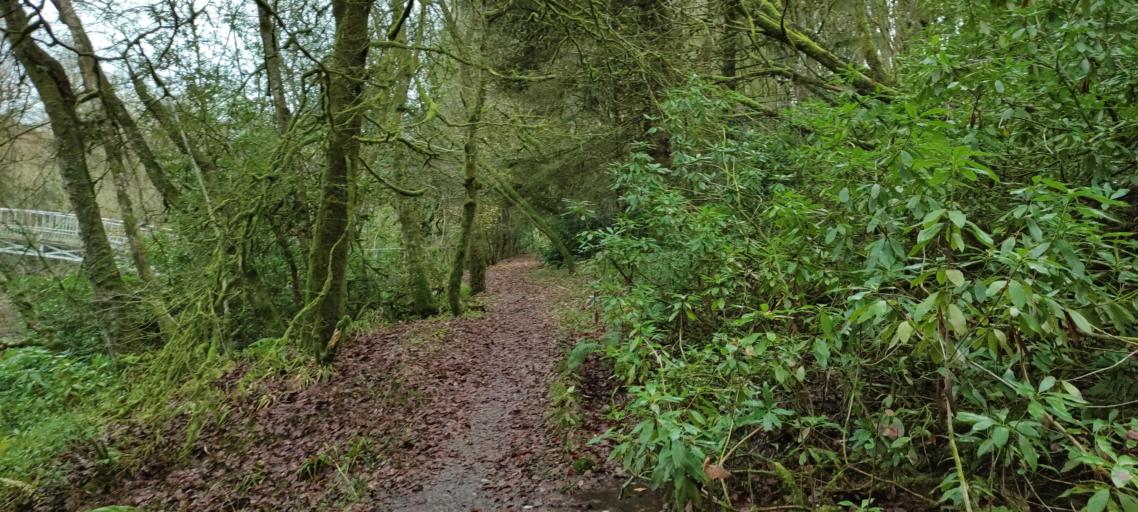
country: GB
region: Scotland
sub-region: Dumfries and Galloway
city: Langholm
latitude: 55.1572
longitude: -3.0131
